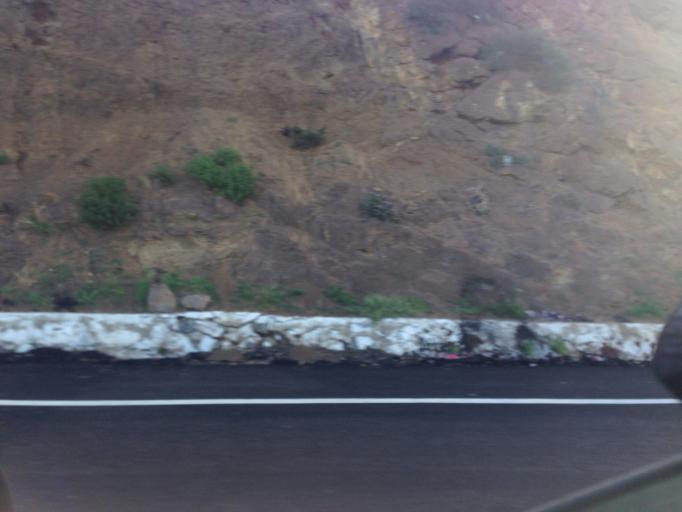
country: MX
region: Baja California
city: Primo Tapia
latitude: 32.1688
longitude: -116.9027
